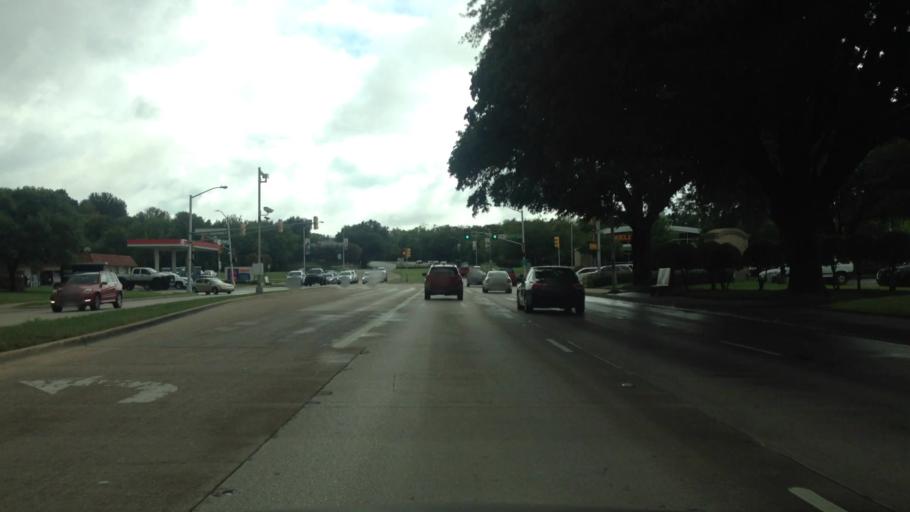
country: US
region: Texas
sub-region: Tarrant County
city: Westworth
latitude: 32.7052
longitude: -97.3887
